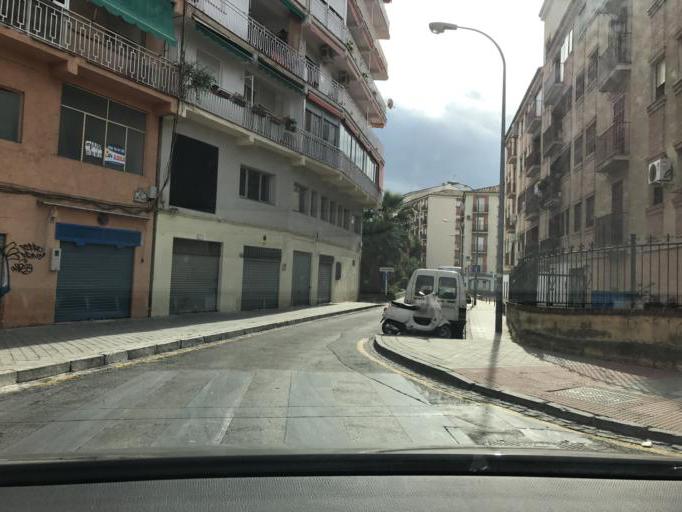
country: ES
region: Andalusia
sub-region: Provincia de Granada
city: Granada
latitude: 37.1654
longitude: -3.6008
